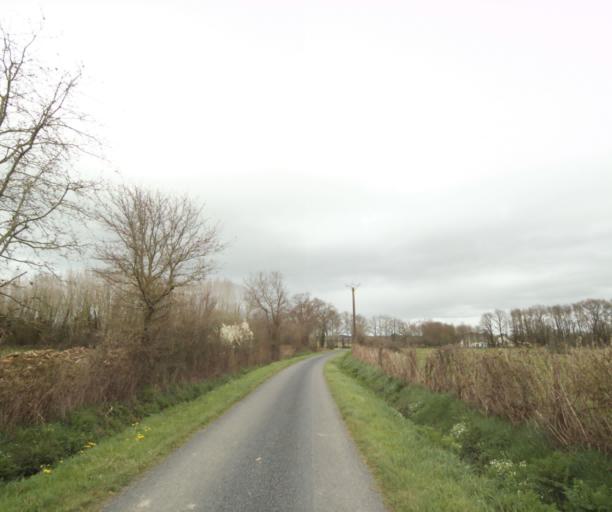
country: FR
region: Pays de la Loire
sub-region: Departement de la Loire-Atlantique
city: Bouvron
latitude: 47.4351
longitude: -1.8470
